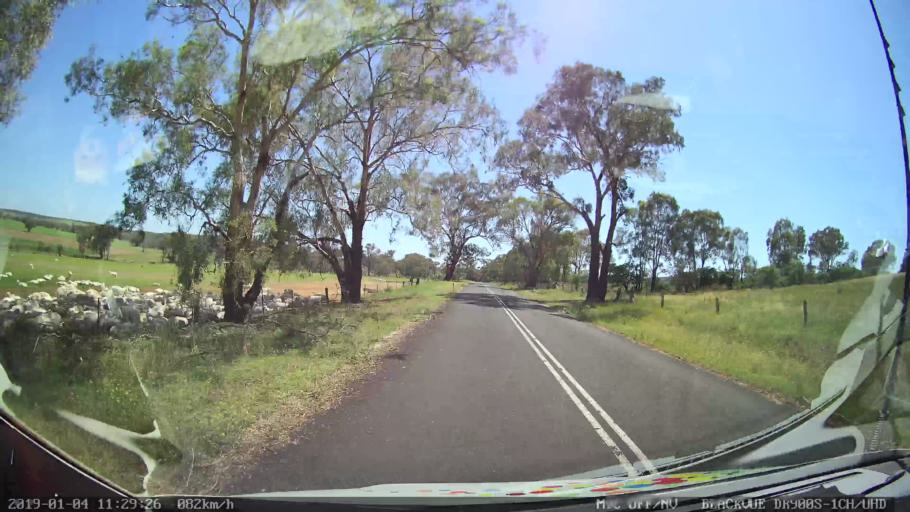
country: AU
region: New South Wales
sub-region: Cabonne
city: Molong
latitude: -33.0879
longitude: 148.7742
